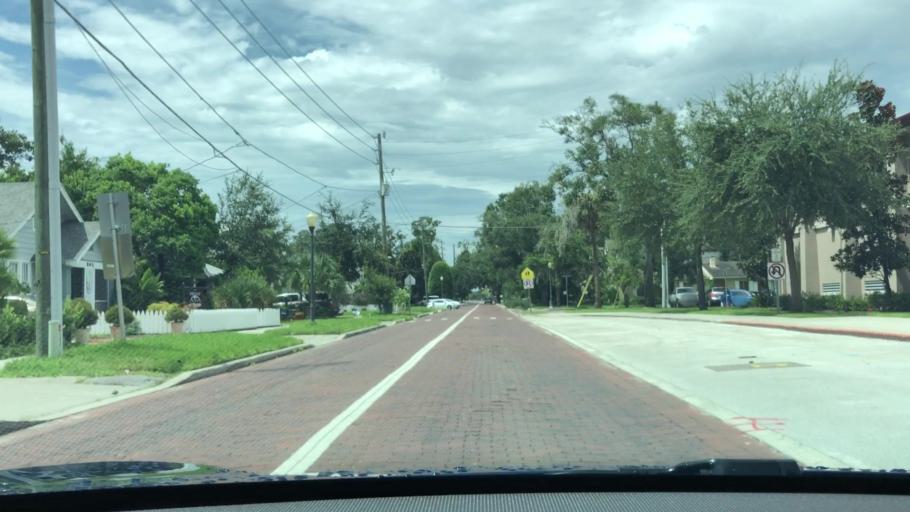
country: US
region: Florida
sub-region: Orange County
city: Winter Park
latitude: 28.5898
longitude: -81.3567
